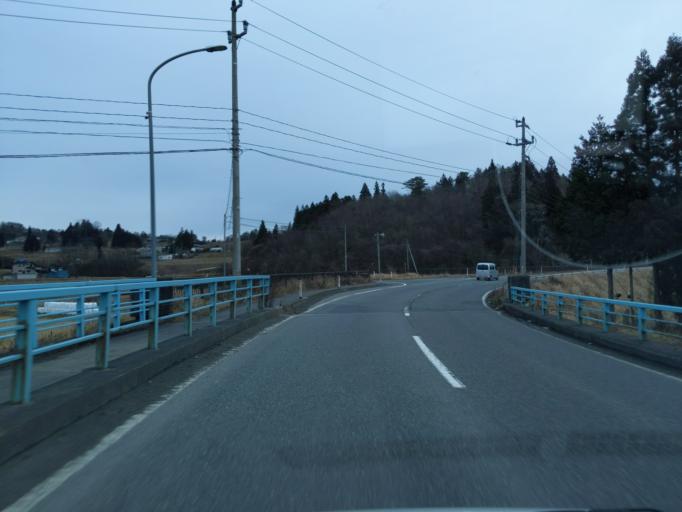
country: JP
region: Iwate
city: Mizusawa
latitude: 39.0264
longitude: 141.3194
